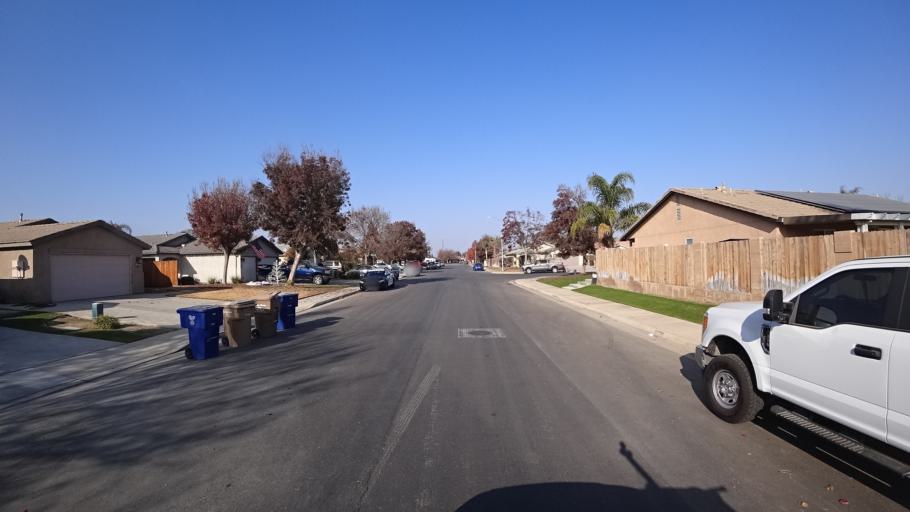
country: US
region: California
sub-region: Kern County
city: Greenacres
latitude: 35.3914
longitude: -119.0694
